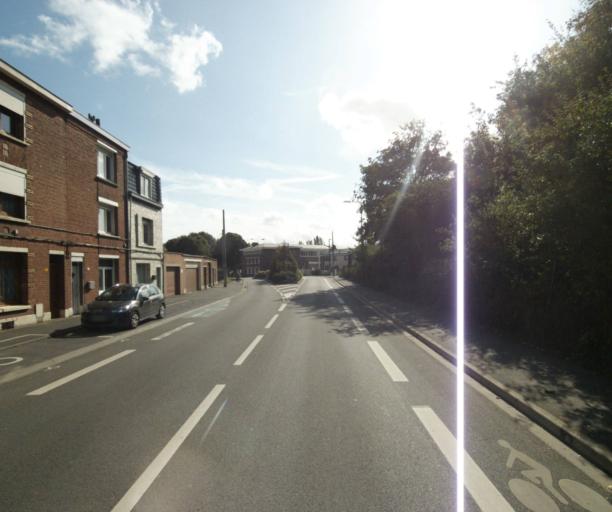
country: FR
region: Nord-Pas-de-Calais
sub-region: Departement du Nord
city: Lomme
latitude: 50.6351
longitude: 3.0045
